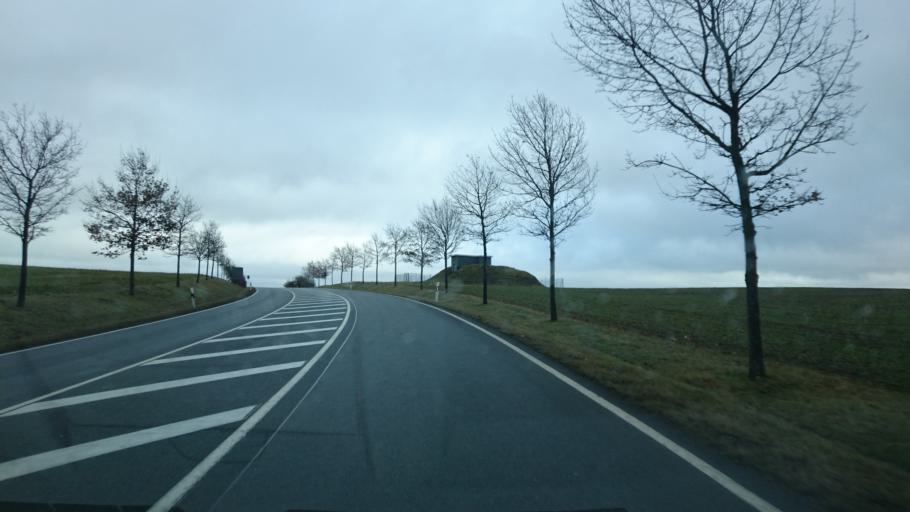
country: DE
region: Thuringia
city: Tanna
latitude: 50.5313
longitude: 11.8744
